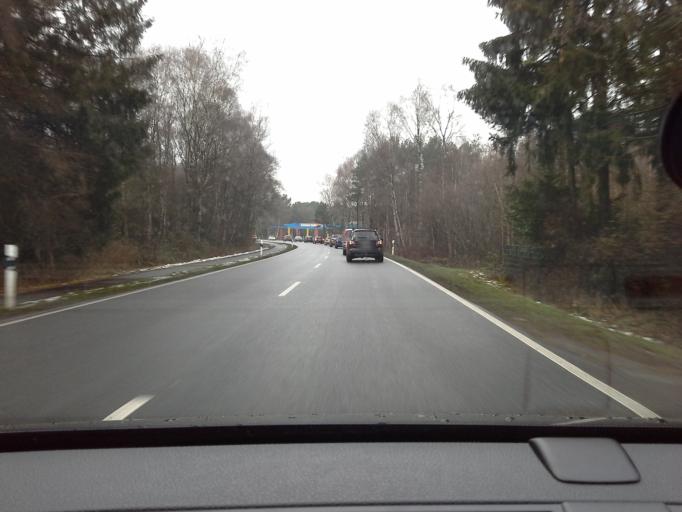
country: DE
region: Schleswig-Holstein
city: Henstedt-Ulzburg
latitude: 53.7478
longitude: 10.0013
